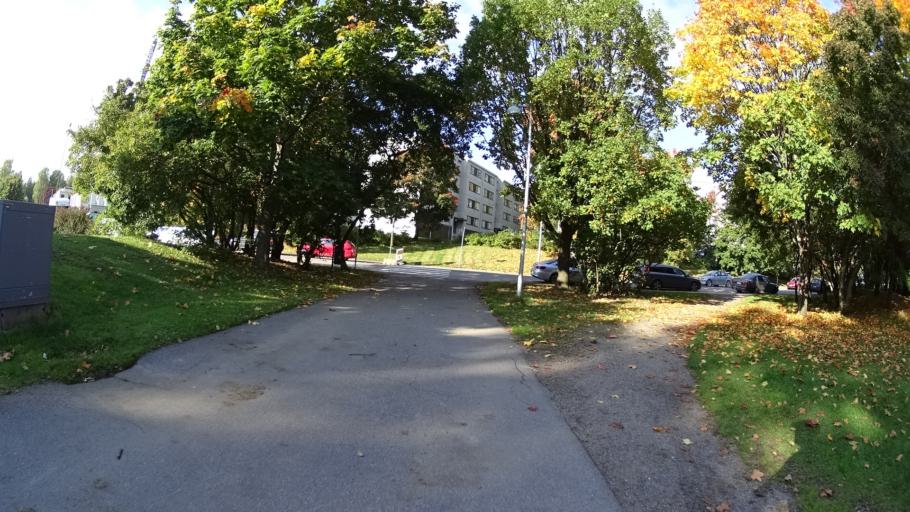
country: FI
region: Uusimaa
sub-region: Helsinki
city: Teekkarikylae
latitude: 60.2329
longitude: 24.8519
